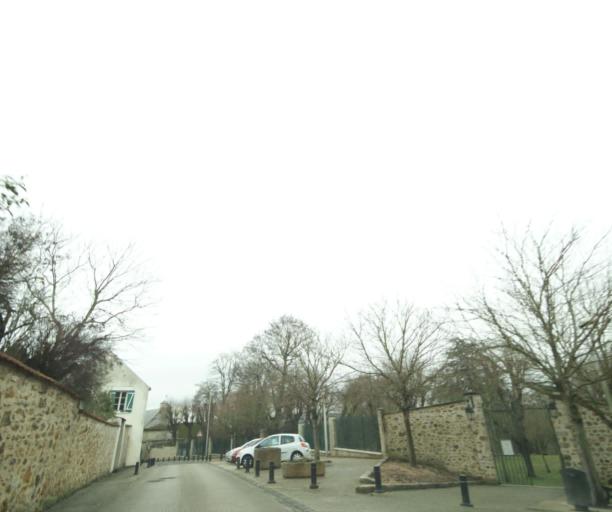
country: FR
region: Ile-de-France
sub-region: Departement de l'Essonne
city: Champlan
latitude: 48.7072
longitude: 2.2715
